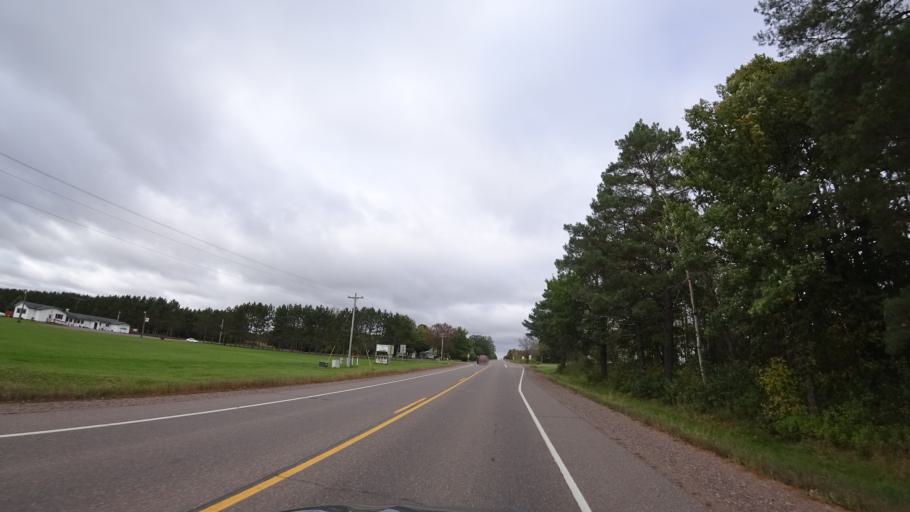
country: US
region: Wisconsin
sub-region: Rusk County
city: Ladysmith
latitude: 45.5075
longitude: -91.1115
